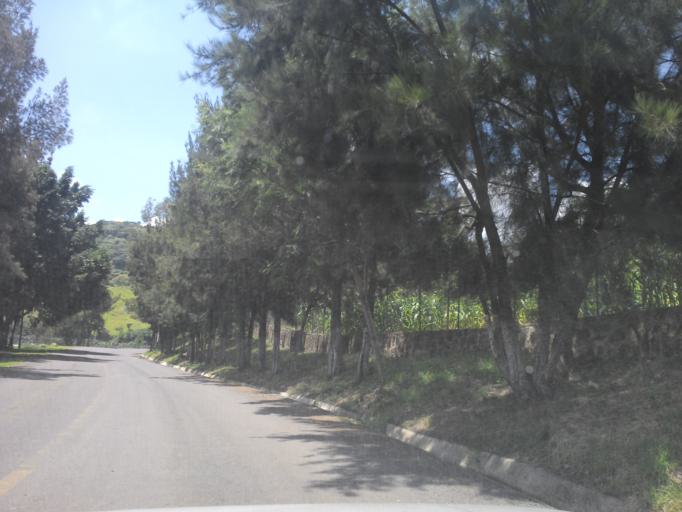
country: MX
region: Jalisco
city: Atotonilco el Alto
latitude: 20.5680
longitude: -102.5121
